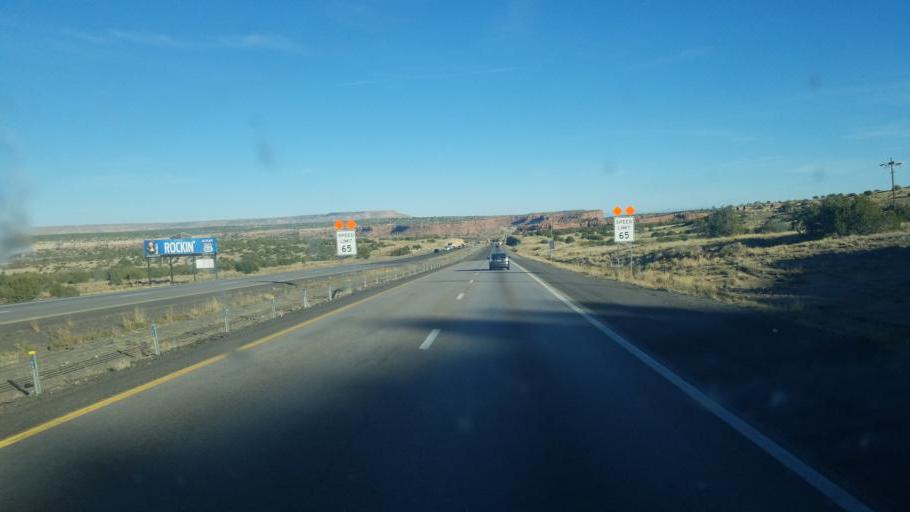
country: US
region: New Mexico
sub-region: Cibola County
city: Laguna
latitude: 35.0378
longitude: -107.3584
